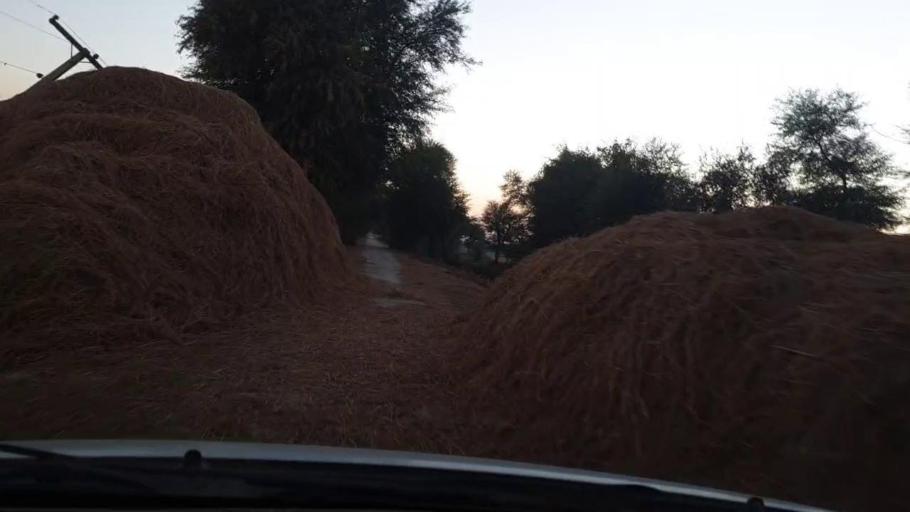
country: PK
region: Sindh
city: Khairpur Nathan Shah
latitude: 27.1498
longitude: 67.6903
